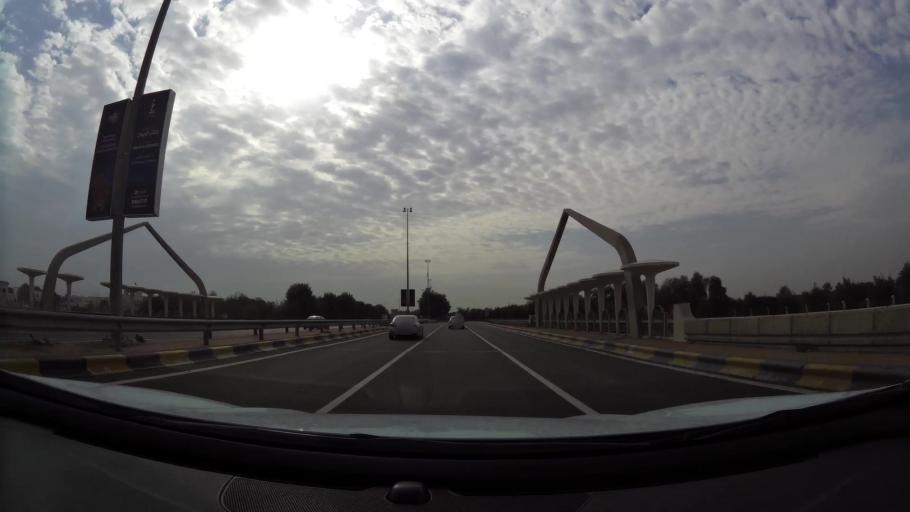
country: AE
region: Abu Dhabi
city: Al Ain
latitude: 24.1800
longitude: 55.6000
